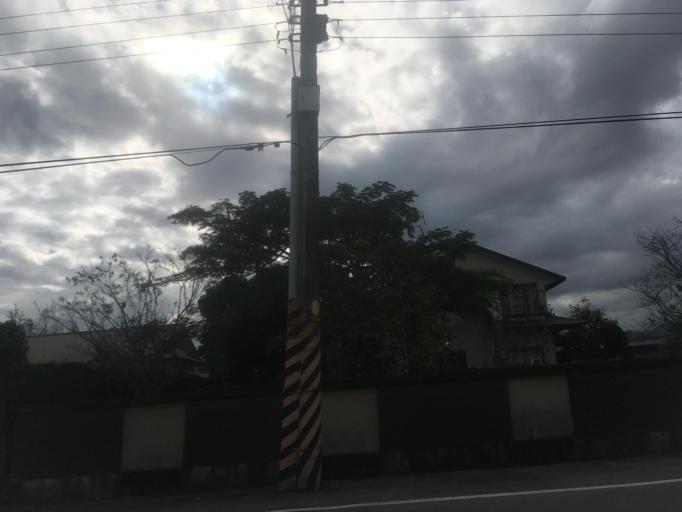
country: TW
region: Taiwan
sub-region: Yilan
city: Yilan
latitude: 24.6893
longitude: 121.7227
